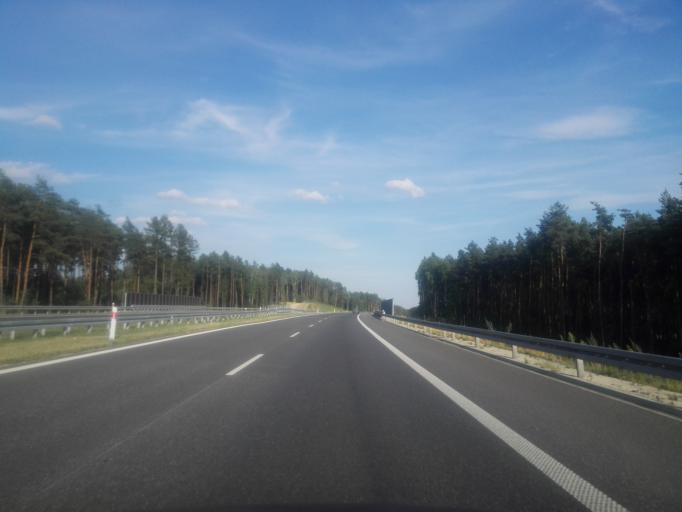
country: PL
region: Greater Poland Voivodeship
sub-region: Powiat kepinski
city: Perzow
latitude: 51.3028
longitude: 17.7964
